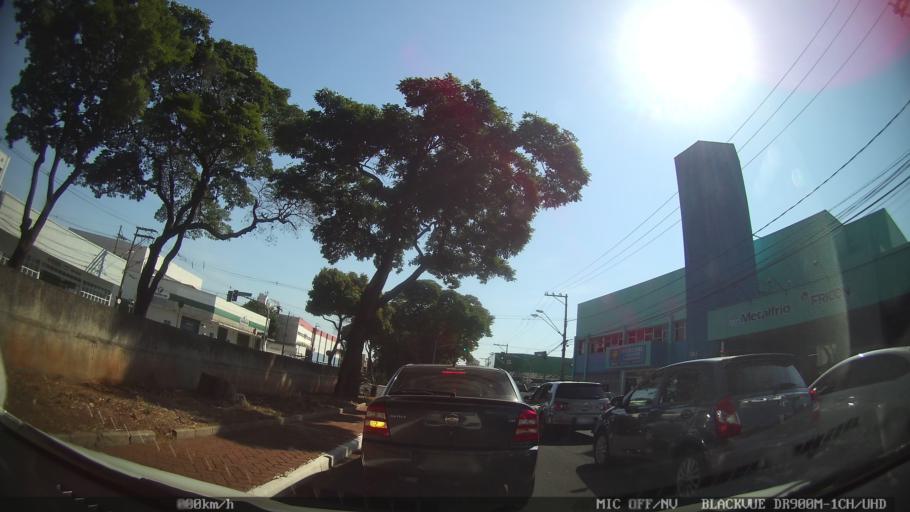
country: BR
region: Sao Paulo
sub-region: Ribeirao Preto
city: Ribeirao Preto
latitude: -21.1768
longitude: -47.8019
